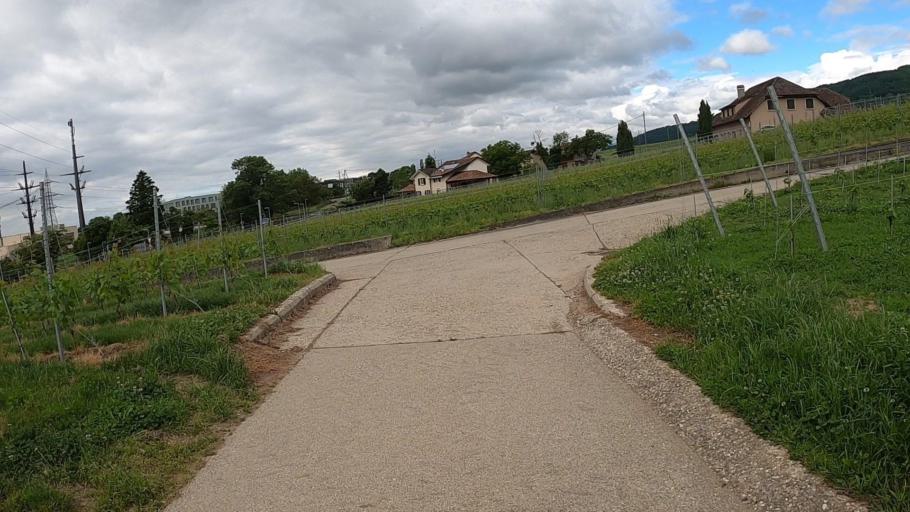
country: CH
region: Vaud
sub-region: Nyon District
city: Rolle
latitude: 46.4640
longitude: 6.3266
